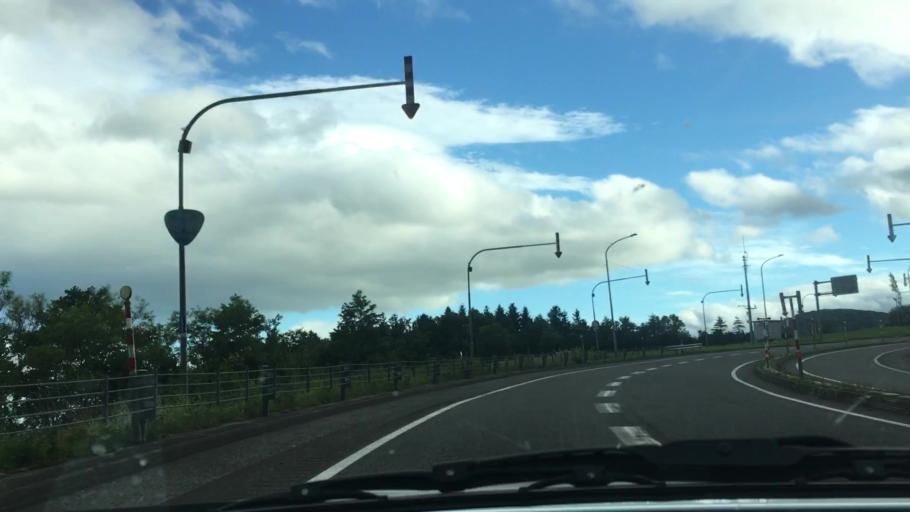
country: JP
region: Hokkaido
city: Otofuke
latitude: 43.1621
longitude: 142.8040
